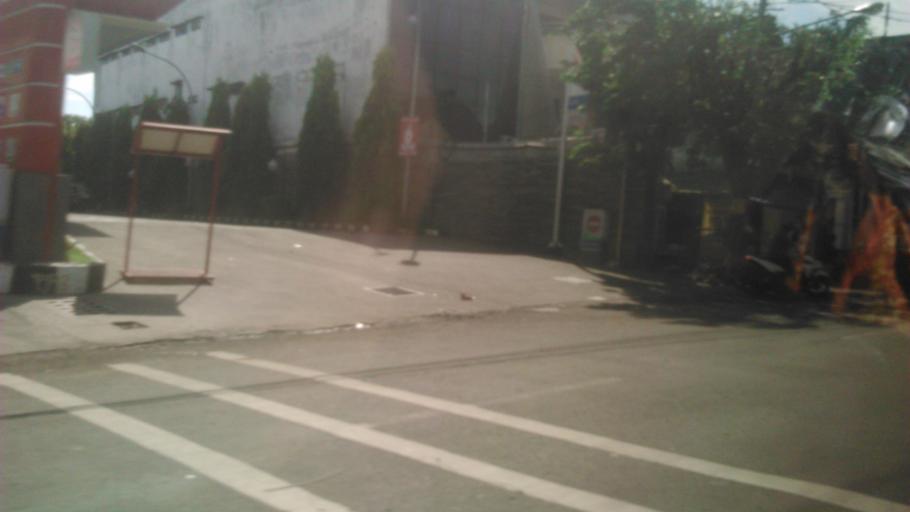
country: ID
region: East Java
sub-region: Kota Surabaya
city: Surabaya
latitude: -7.2492
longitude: 112.7547
